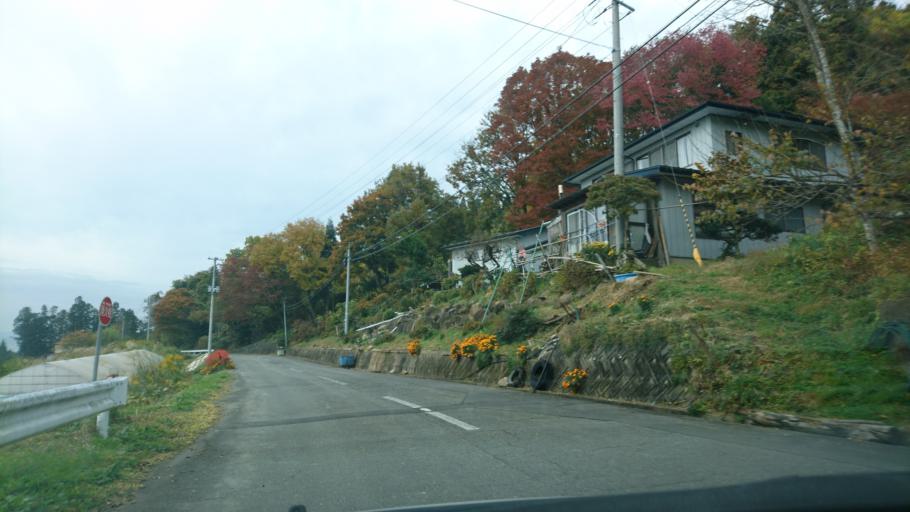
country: JP
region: Iwate
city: Ichinoseki
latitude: 38.9792
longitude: 141.1695
